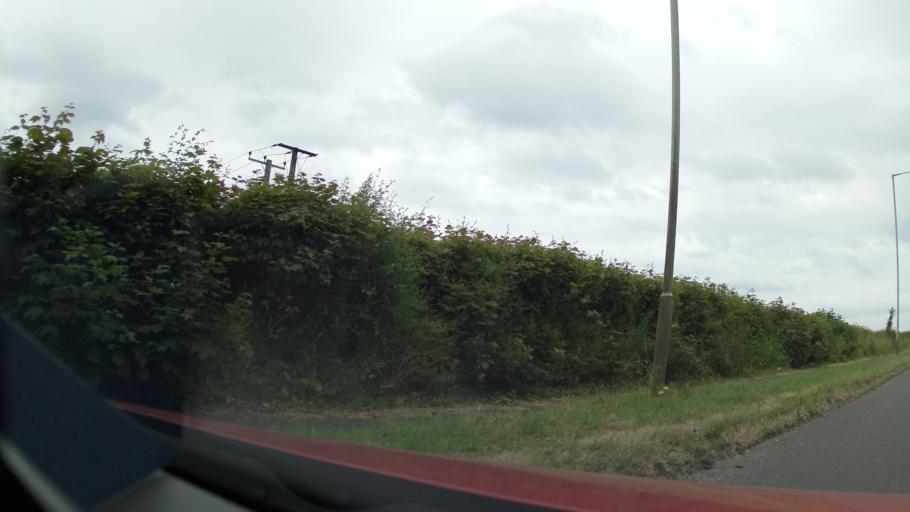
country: GB
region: England
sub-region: Staffordshire
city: Penkridge
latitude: 52.7566
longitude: -2.1075
